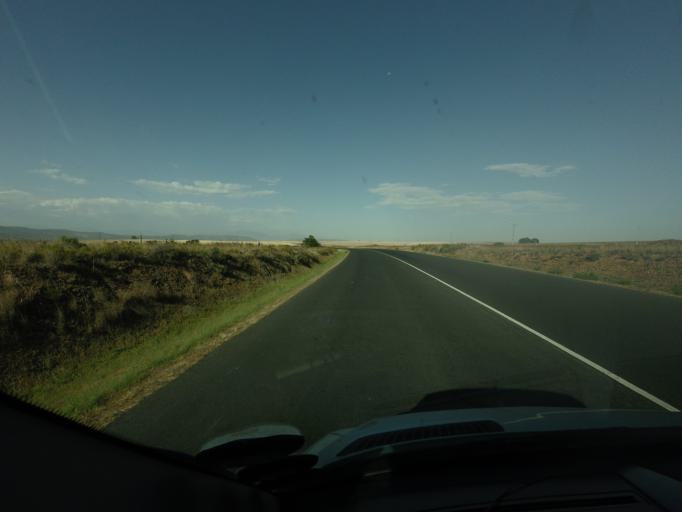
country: ZA
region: Western Cape
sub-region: Cape Winelands District Municipality
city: Ashton
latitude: -34.1405
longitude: 20.0193
